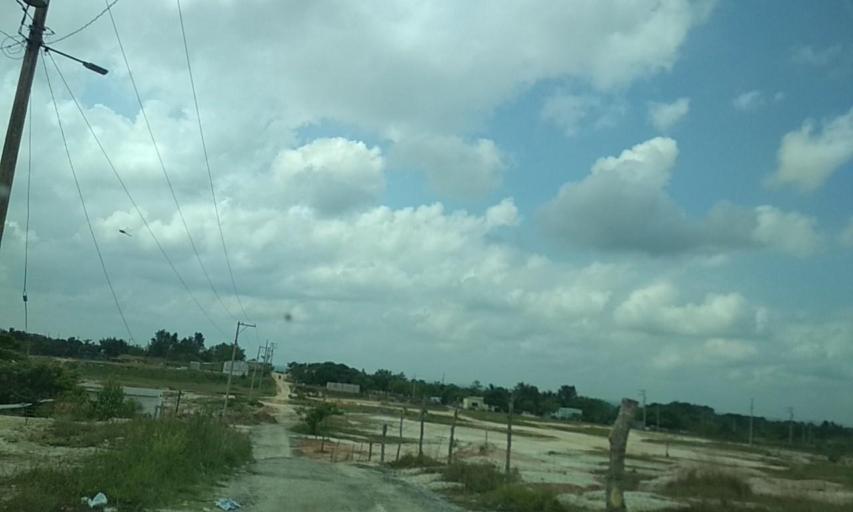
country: MX
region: Veracruz
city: Las Choapas
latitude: 17.9015
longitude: -94.1167
